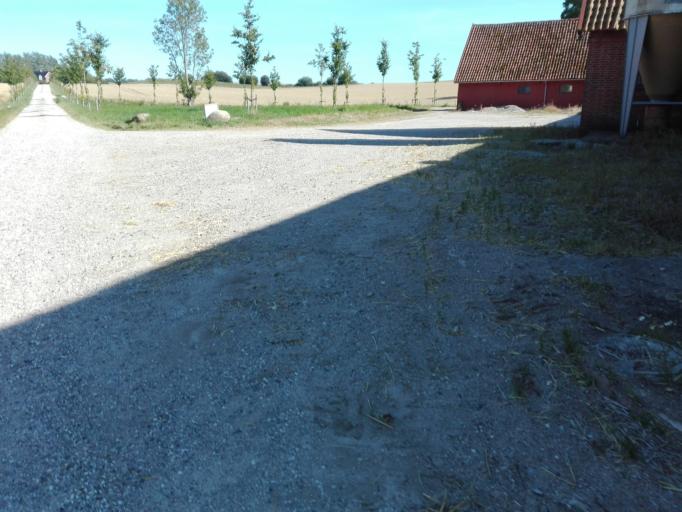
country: DK
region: Central Jutland
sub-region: Odder Kommune
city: Odder
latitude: 55.9545
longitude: 10.1053
